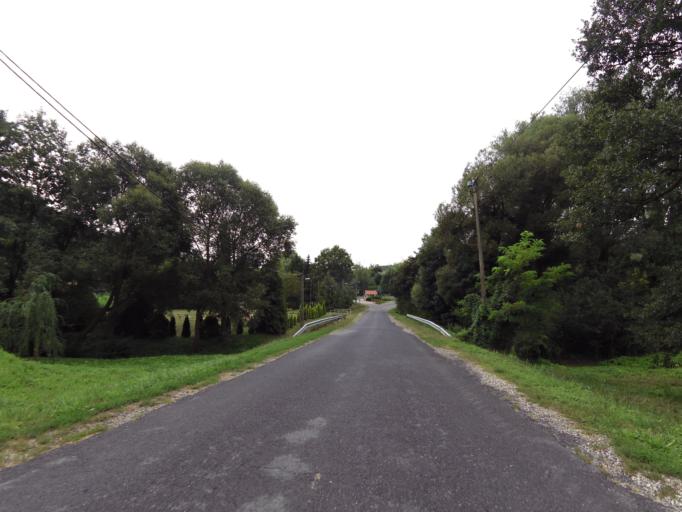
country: HU
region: Zala
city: Gyenesdias
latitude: 46.8463
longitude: 17.3035
